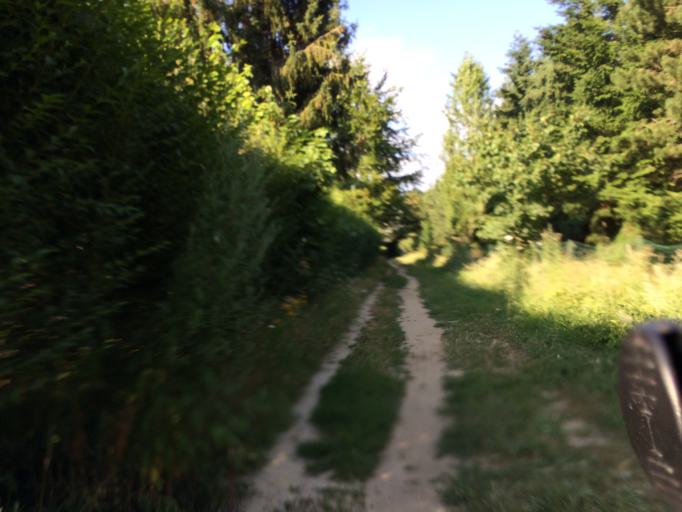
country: FR
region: Ile-de-France
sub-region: Departement de l'Essonne
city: Soisy-sur-Seine
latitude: 48.6489
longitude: 2.4677
